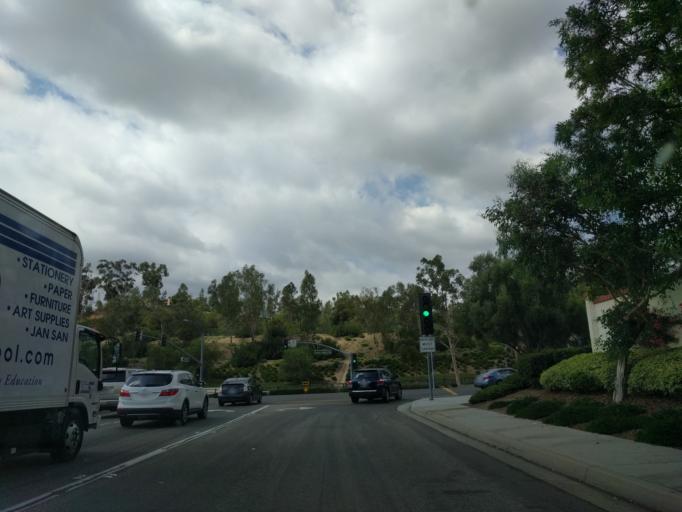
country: US
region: California
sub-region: Orange County
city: North Tustin
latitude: 33.7469
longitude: -117.7737
